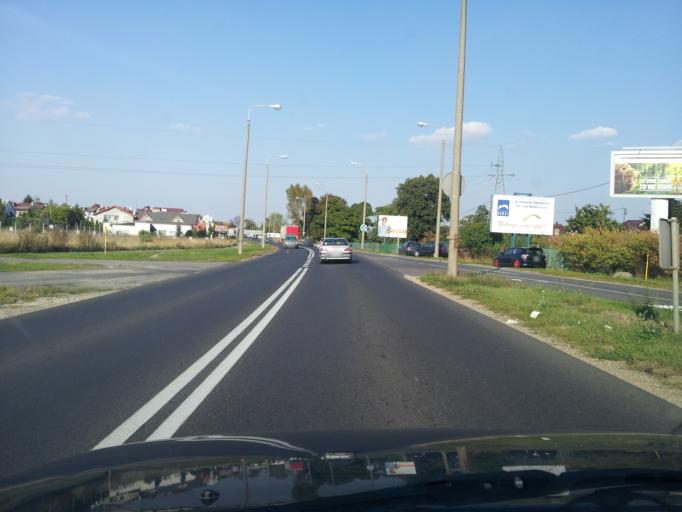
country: PL
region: Kujawsko-Pomorskie
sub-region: Torun
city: Torun
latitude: 52.9774
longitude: 18.5695
